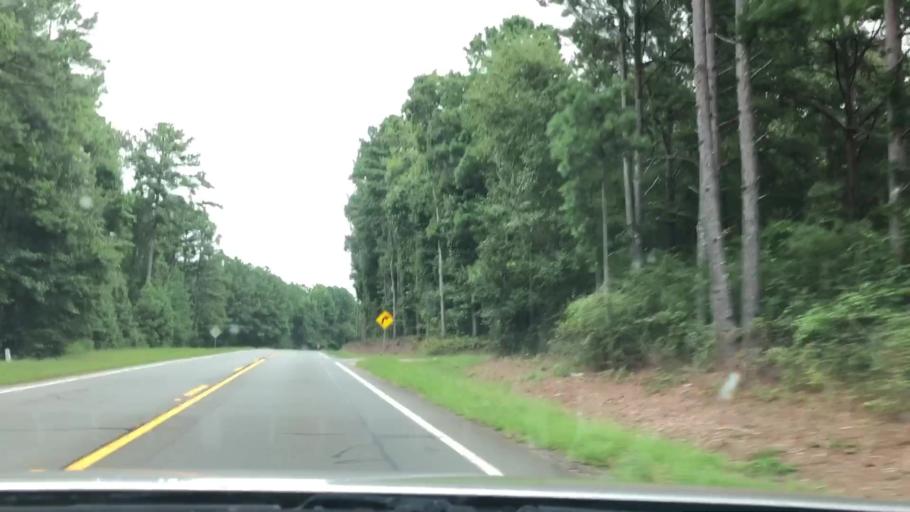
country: US
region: Georgia
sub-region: Pike County
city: Zebulon
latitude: 33.1005
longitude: -84.4246
